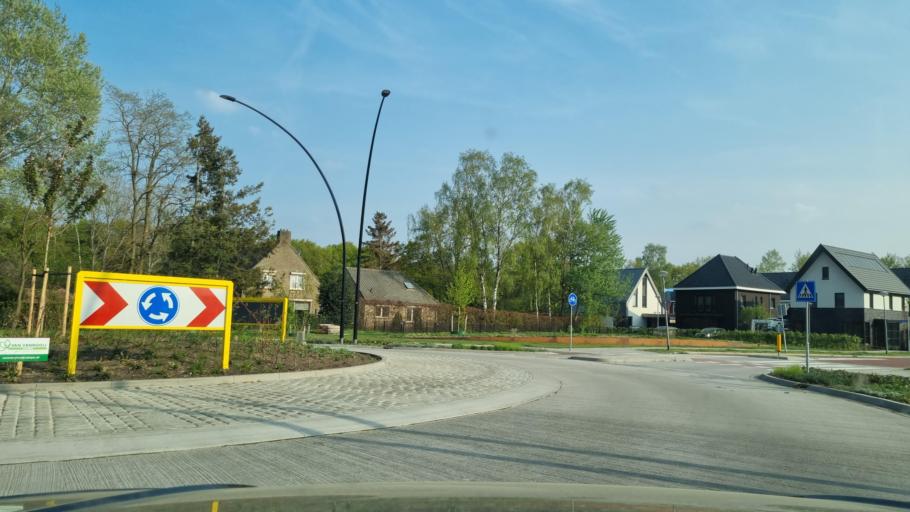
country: NL
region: North Brabant
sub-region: Gemeente Bernheze
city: Heesch
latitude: 51.7355
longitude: 5.5476
